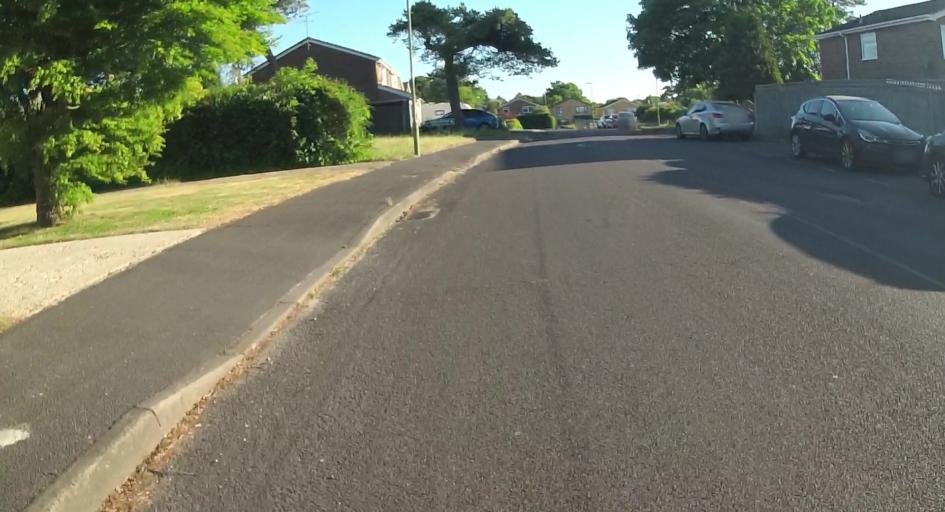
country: GB
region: England
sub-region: Hampshire
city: Basingstoke
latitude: 51.2484
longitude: -1.1338
